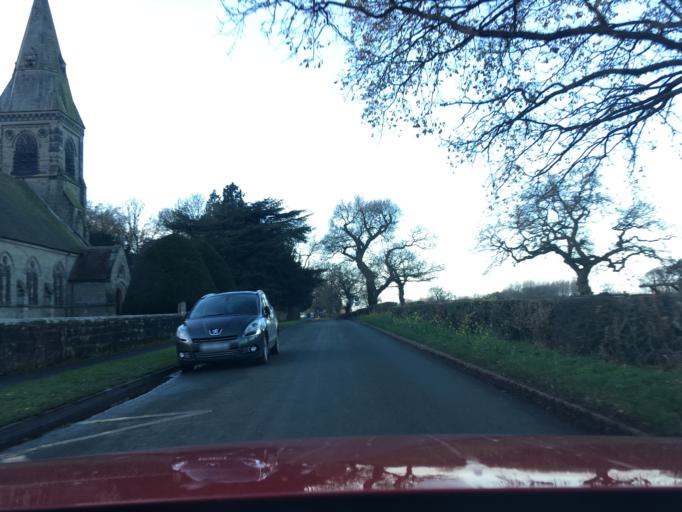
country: GB
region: England
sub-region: Staffordshire
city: Barton under Needwood
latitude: 52.8041
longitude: -1.7331
